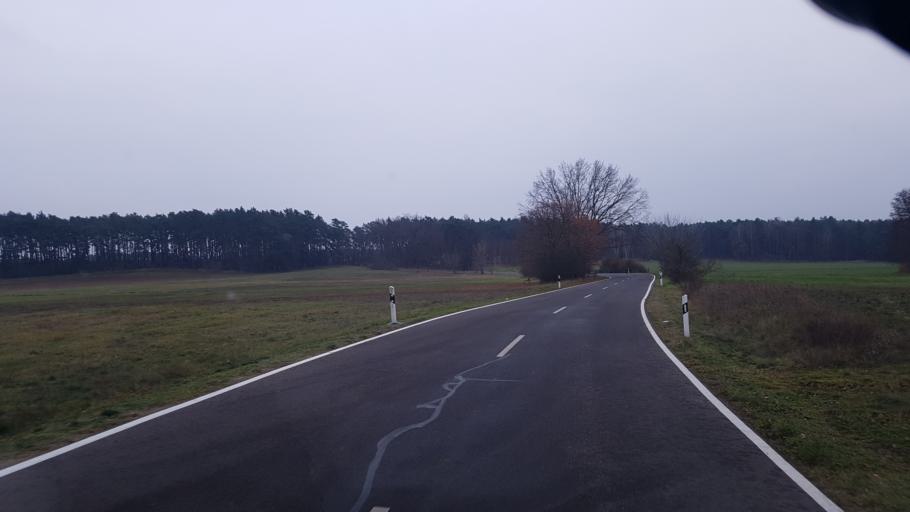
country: DE
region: Brandenburg
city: Schenkendobern
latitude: 51.9645
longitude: 14.6587
